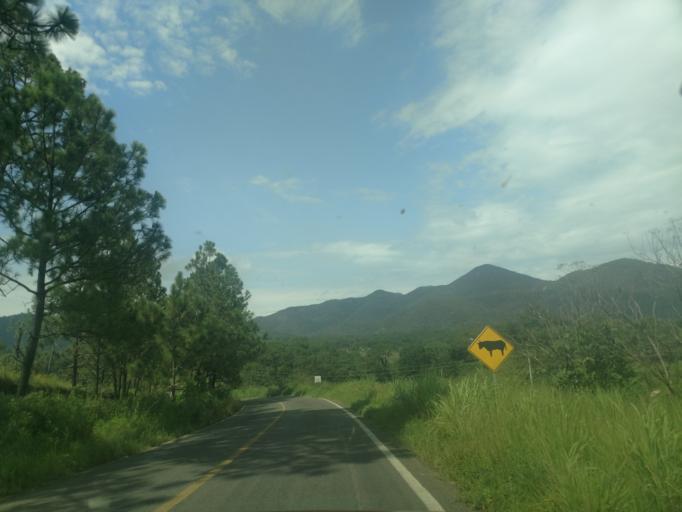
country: MX
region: Jalisco
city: Mascota
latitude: 20.4445
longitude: -104.7621
